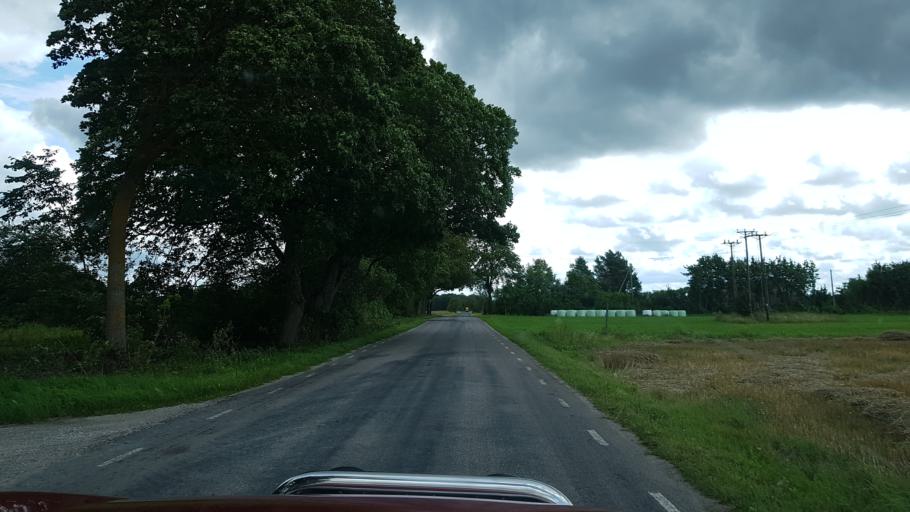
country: EE
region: Laeaene
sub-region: Lihula vald
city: Lihula
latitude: 58.7117
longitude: 24.0087
